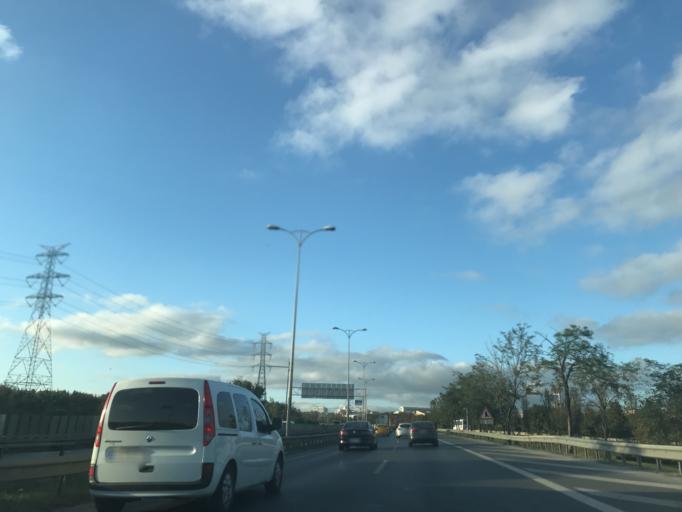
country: TR
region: Istanbul
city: Esenler
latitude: 41.0590
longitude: 28.8859
